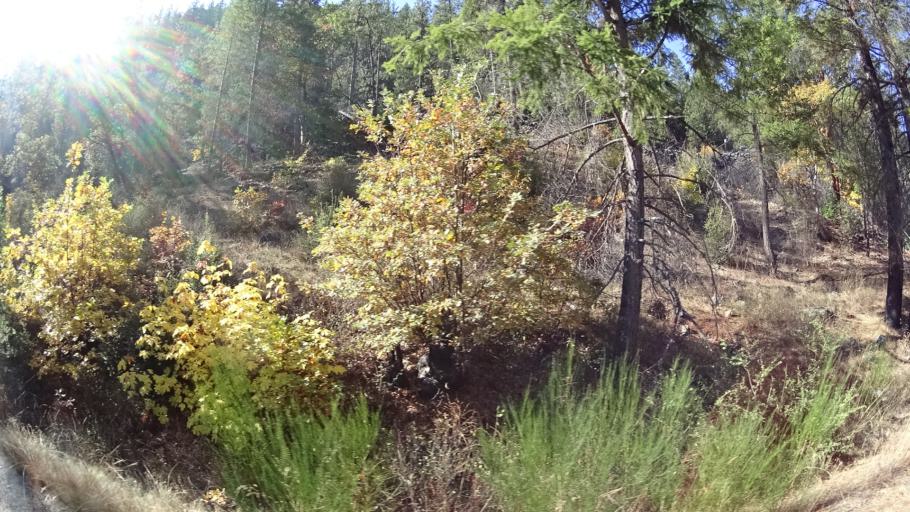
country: US
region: California
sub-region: Siskiyou County
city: Happy Camp
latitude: 41.7717
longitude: -123.0286
